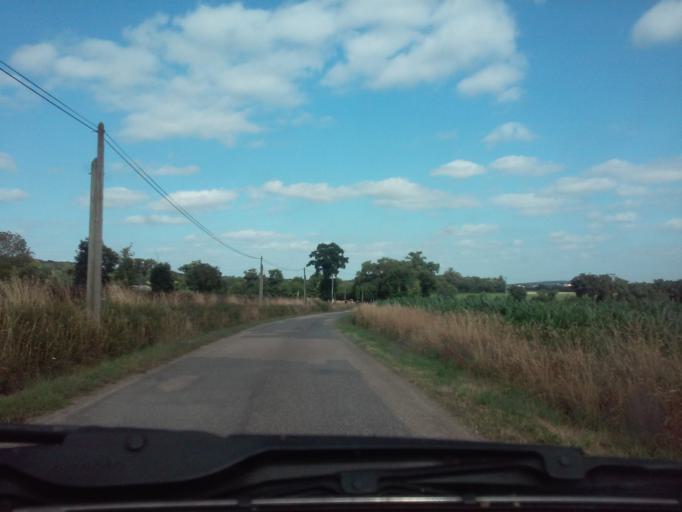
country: FR
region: Brittany
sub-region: Departement d'Ille-et-Vilaine
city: Plechatel
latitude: 47.9120
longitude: -1.7492
